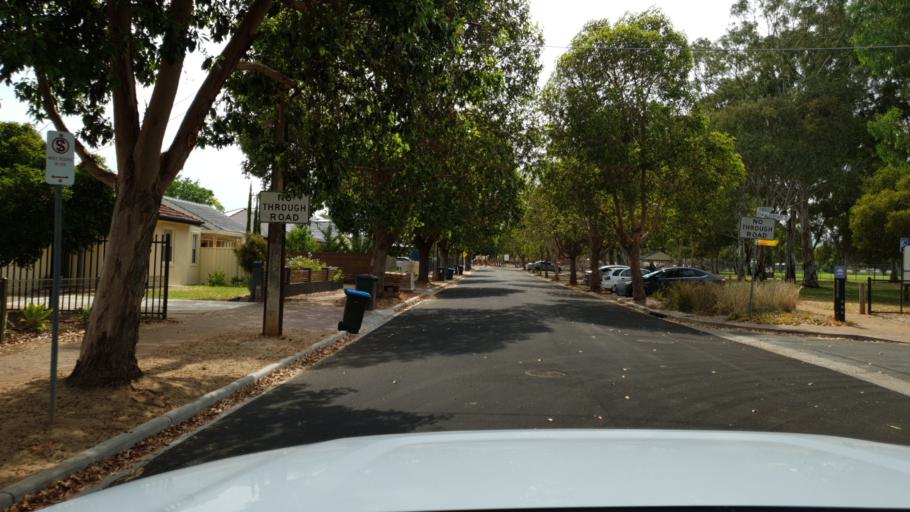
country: AU
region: South Australia
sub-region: Mitcham
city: Clarence Gardens
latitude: -34.9725
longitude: 138.5758
